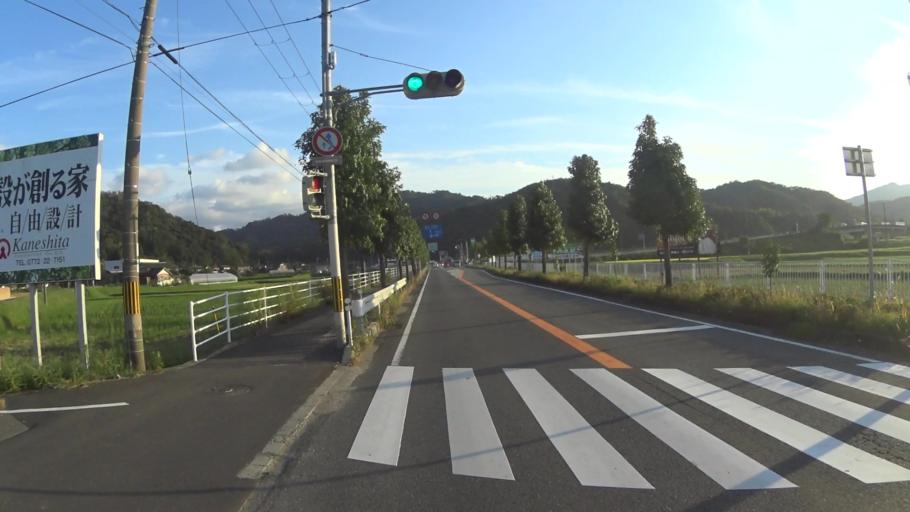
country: JP
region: Kyoto
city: Miyazu
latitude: 35.5697
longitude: 135.0970
